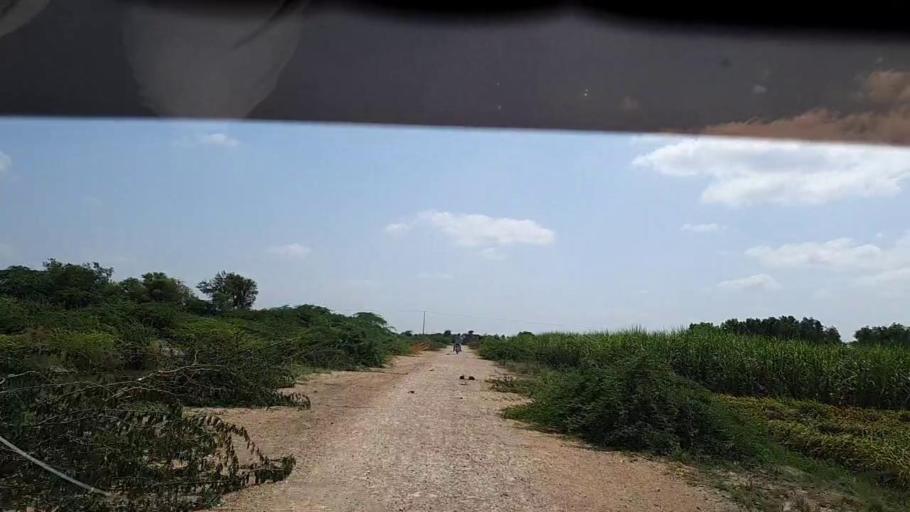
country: PK
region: Sindh
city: Kadhan
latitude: 24.5909
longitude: 68.9922
